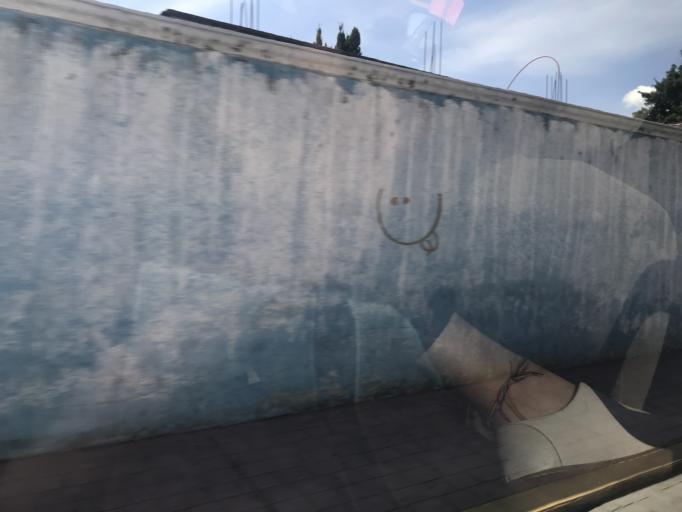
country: MX
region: Puebla
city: San Andres Cholula
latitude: 19.0565
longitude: -98.2953
